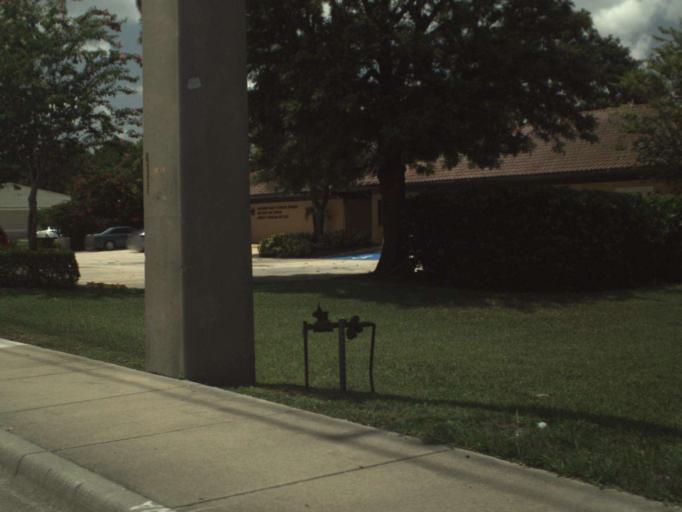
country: US
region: Florida
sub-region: Martin County
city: North River Shores
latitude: 27.2712
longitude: -80.2935
